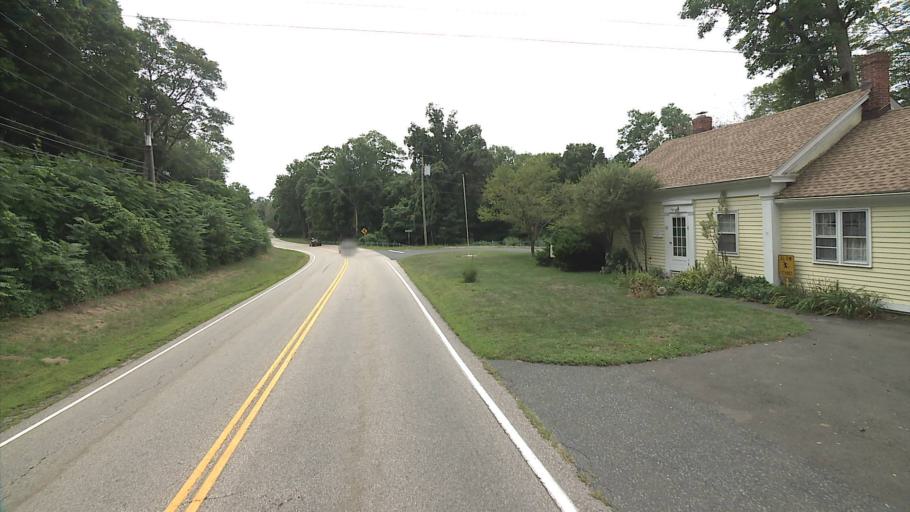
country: US
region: Connecticut
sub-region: Middlesex County
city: Essex Village
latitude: 41.3683
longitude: -72.3461
